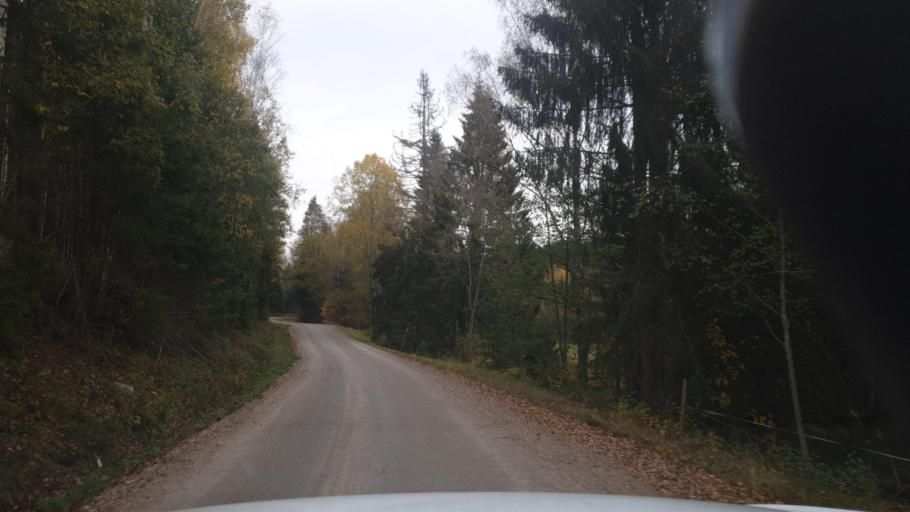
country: SE
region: Vaermland
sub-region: Arvika Kommun
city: Arvika
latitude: 59.6800
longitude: 12.7704
